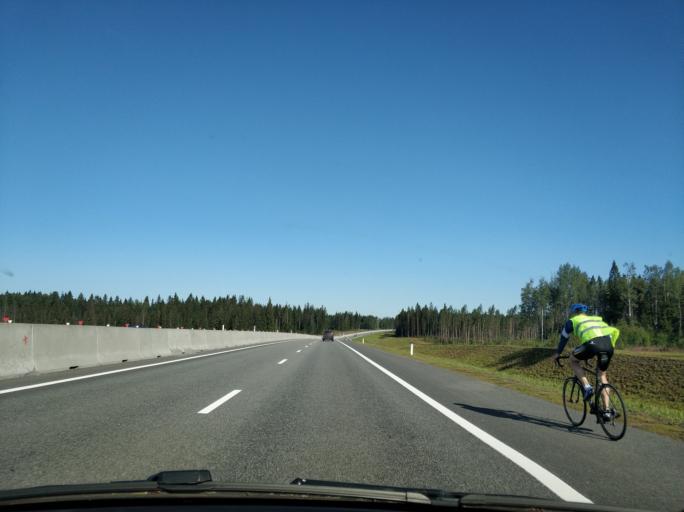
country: RU
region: Leningrad
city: Sosnovo
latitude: 60.5169
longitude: 30.1797
